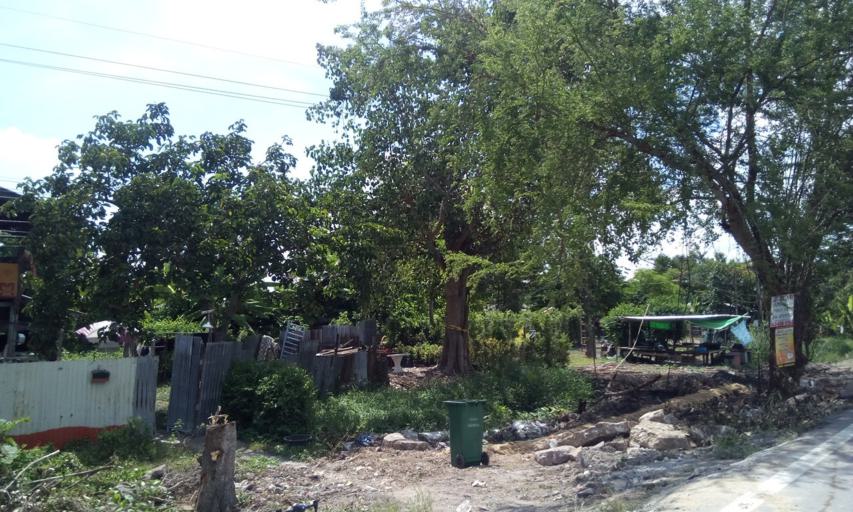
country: TH
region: Nakhon Nayok
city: Ongkharak
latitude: 14.0859
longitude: 100.9145
